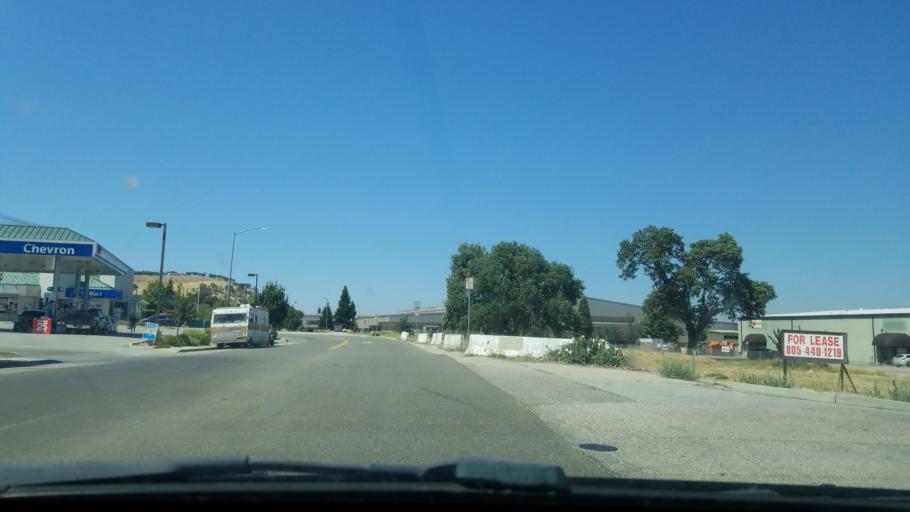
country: US
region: California
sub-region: San Luis Obispo County
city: Paso Robles
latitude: 35.5899
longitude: -120.6946
